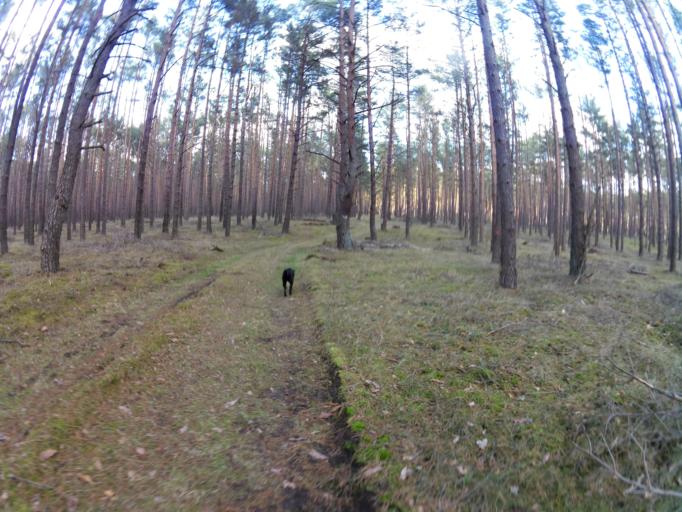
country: PL
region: West Pomeranian Voivodeship
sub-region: Powiat mysliborski
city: Debno
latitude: 52.7823
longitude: 14.7377
